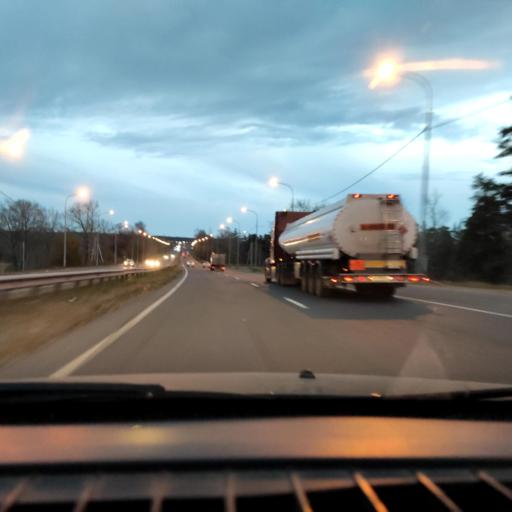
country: RU
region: Samara
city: Zhigulevsk
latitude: 53.5322
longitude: 49.5174
